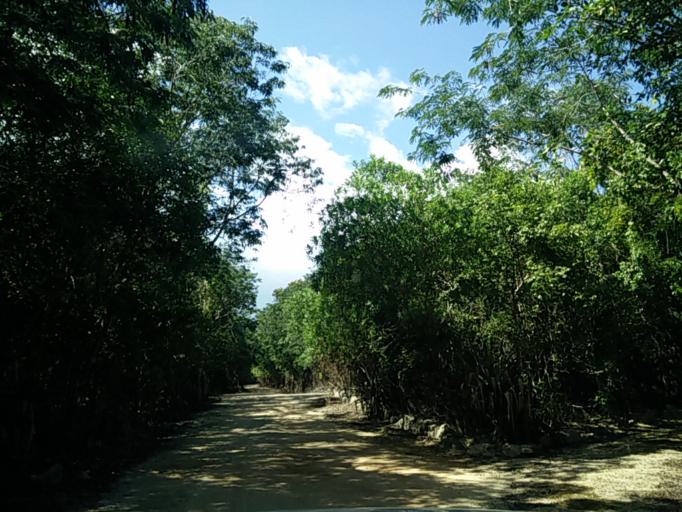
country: MX
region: Quintana Roo
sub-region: Tulum
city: Ciudad Chemuyil
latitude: 20.4973
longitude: -87.2584
